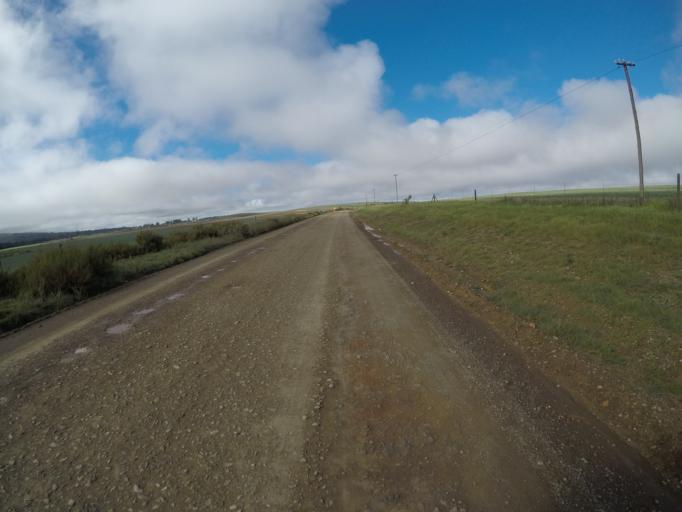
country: ZA
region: Western Cape
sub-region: Cape Winelands District Municipality
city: Ashton
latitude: -34.1506
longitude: 19.8799
